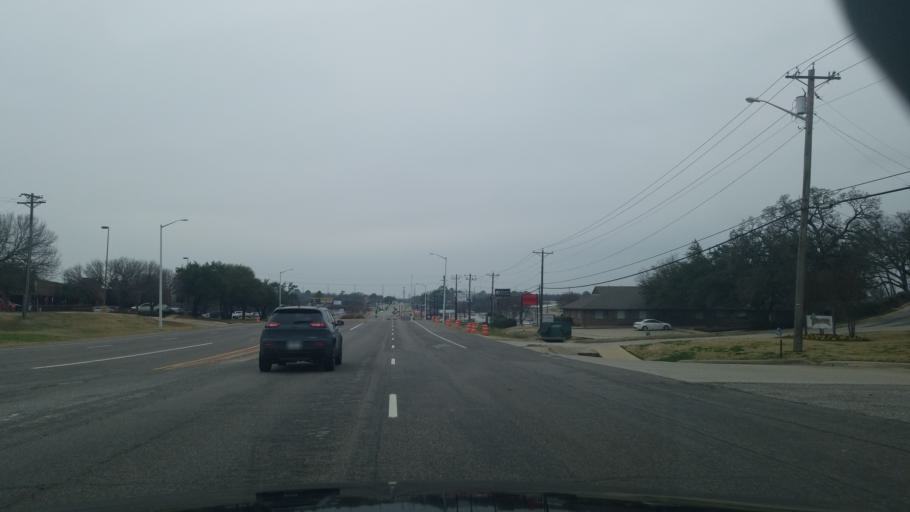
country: US
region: Texas
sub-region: Denton County
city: Denton
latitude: 33.1970
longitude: -97.1212
